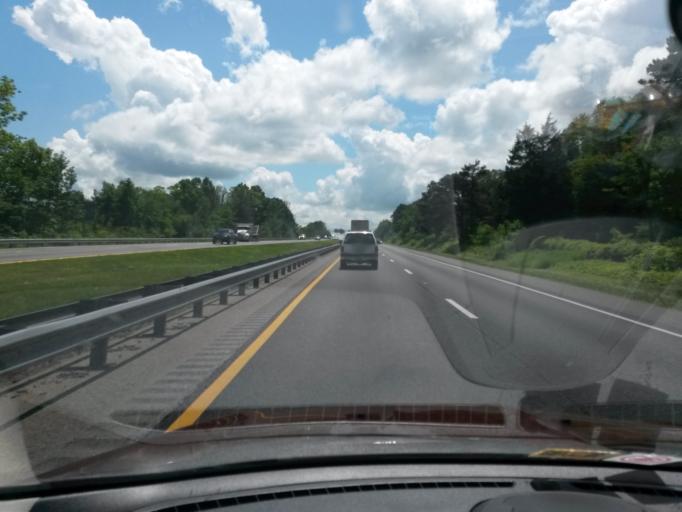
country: US
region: Virginia
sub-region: Pulaski County
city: Pulaski
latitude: 37.0197
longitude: -80.7331
